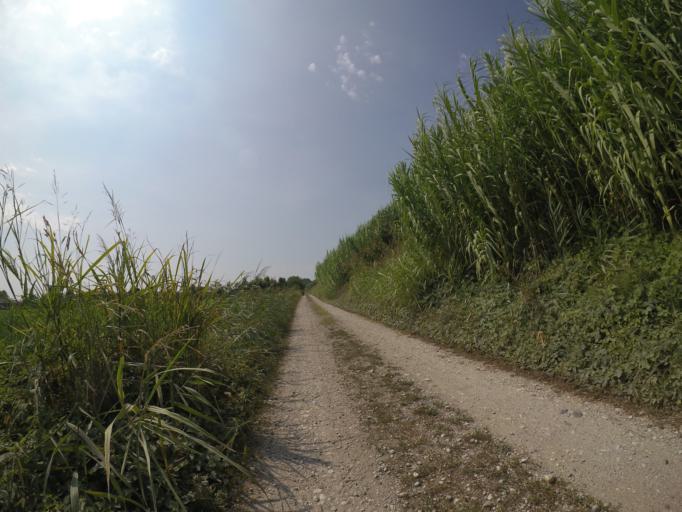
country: IT
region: Friuli Venezia Giulia
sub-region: Provincia di Udine
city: Pertegada
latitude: 45.7173
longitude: 13.0412
